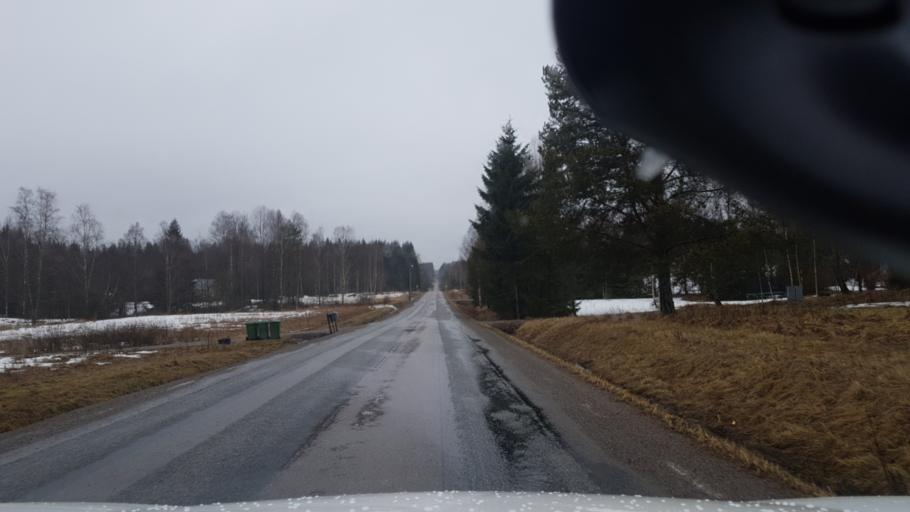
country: SE
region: Vaermland
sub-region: Arvika Kommun
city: Arvika
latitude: 59.6649
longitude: 12.6664
